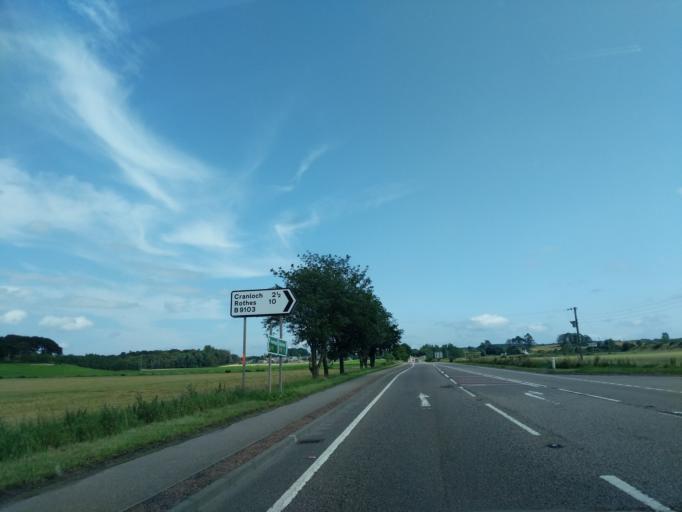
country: GB
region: Scotland
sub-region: Moray
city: Lhanbryd
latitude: 57.6375
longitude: -3.2451
